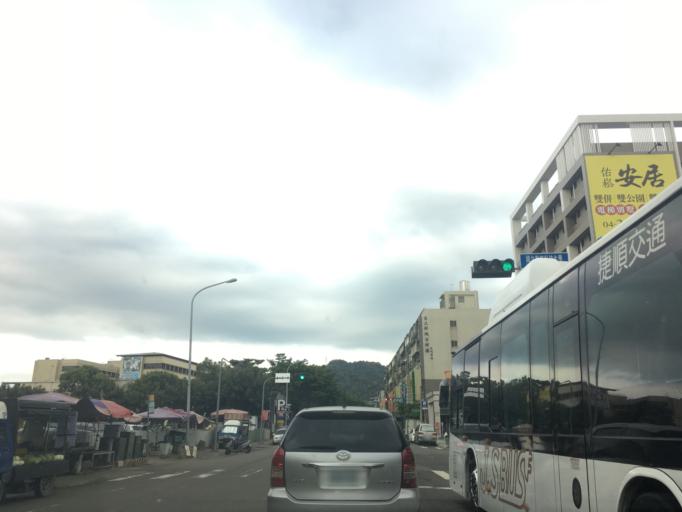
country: TW
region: Taiwan
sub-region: Taichung City
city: Taichung
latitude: 24.1500
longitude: 120.7278
